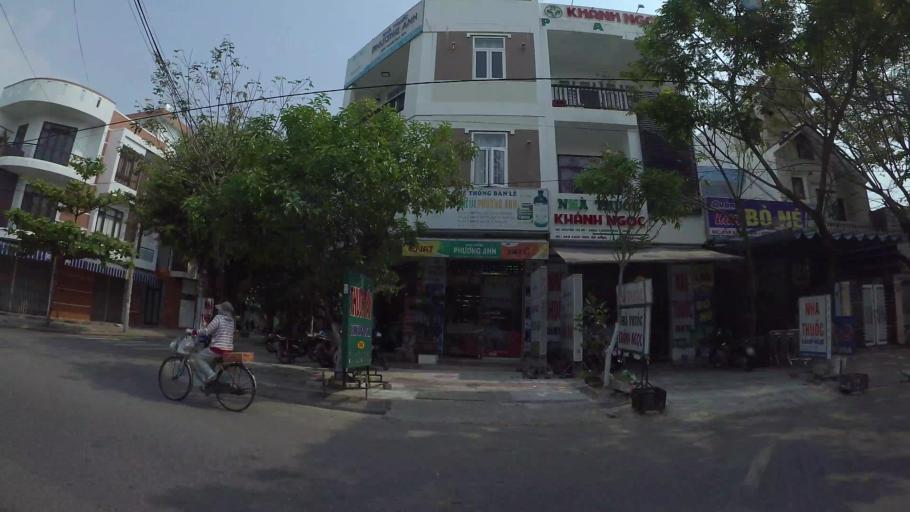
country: VN
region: Da Nang
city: Da Nang
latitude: 16.0945
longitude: 108.2306
